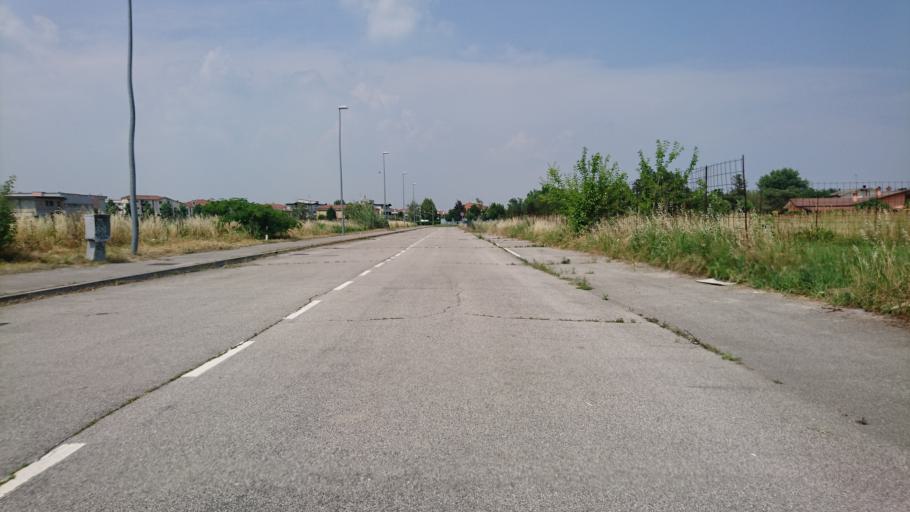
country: IT
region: Veneto
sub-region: Provincia di Padova
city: Masera di Padova
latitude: 45.3137
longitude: 11.8676
